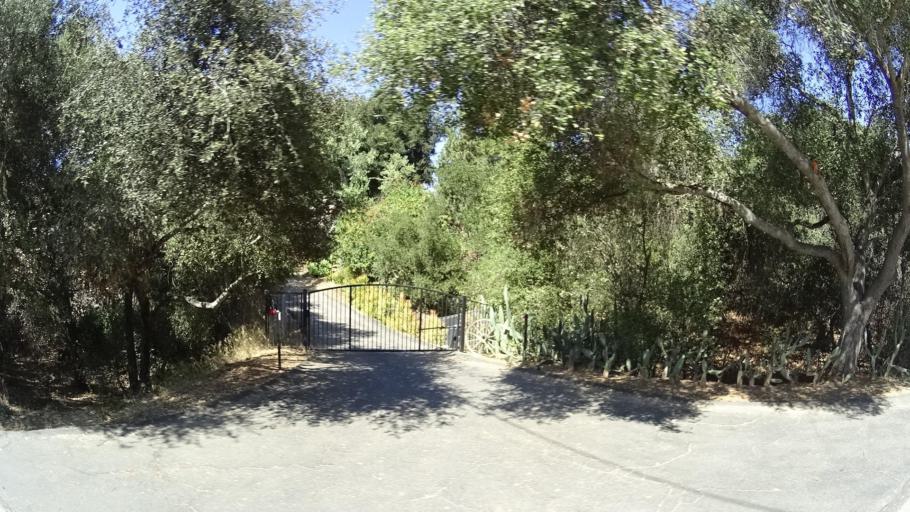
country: US
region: California
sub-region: San Diego County
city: Hidden Meadows
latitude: 33.2830
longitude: -117.1168
